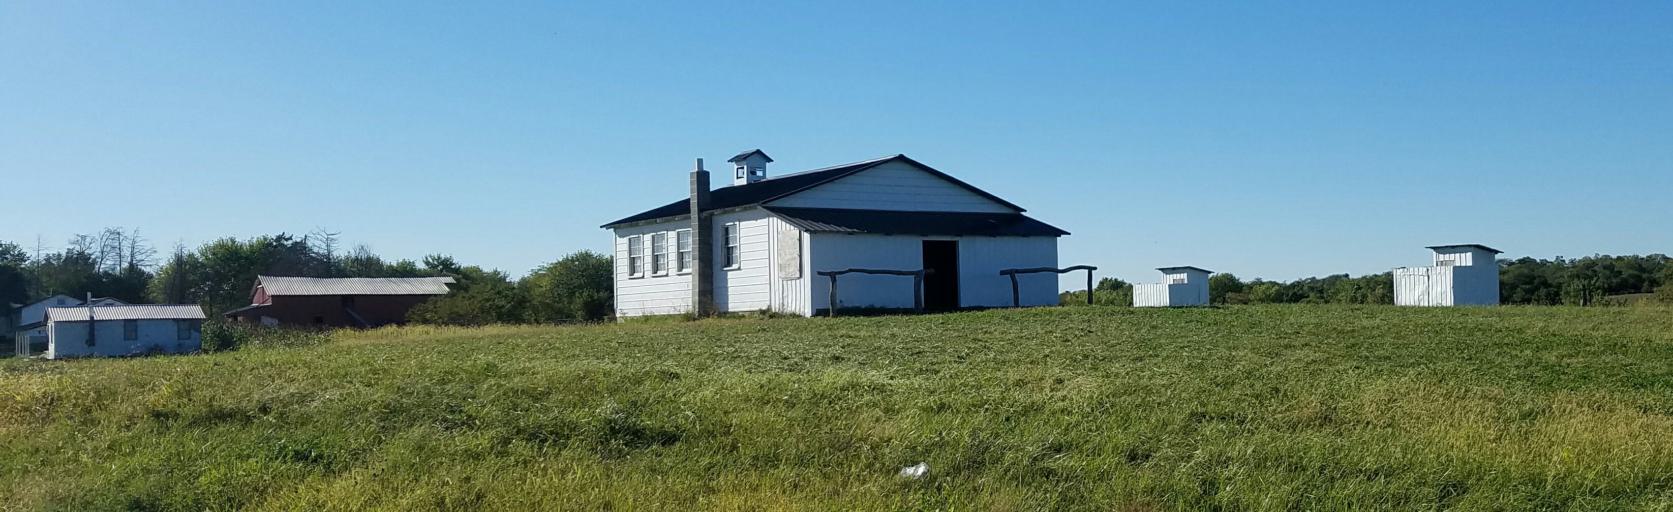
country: US
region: Iowa
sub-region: Decatur County
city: Lamoni
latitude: 40.6382
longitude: -93.8771
